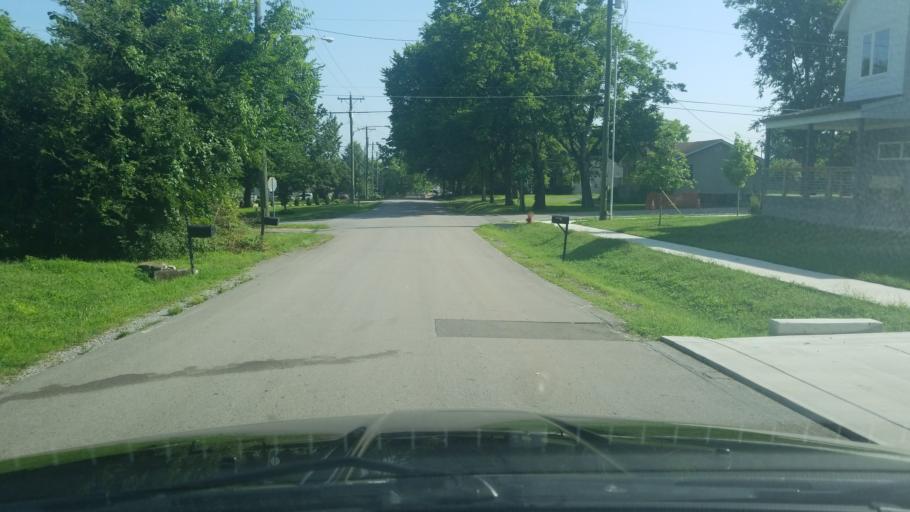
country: US
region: Tennessee
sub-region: Davidson County
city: Belle Meade
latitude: 36.1548
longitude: -86.8662
